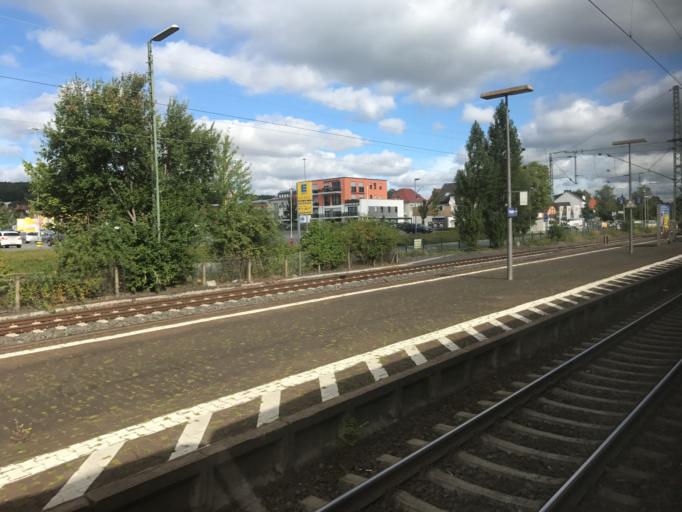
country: DE
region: Hesse
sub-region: Regierungsbezirk Darmstadt
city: Butzbach
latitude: 50.4302
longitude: 8.6698
